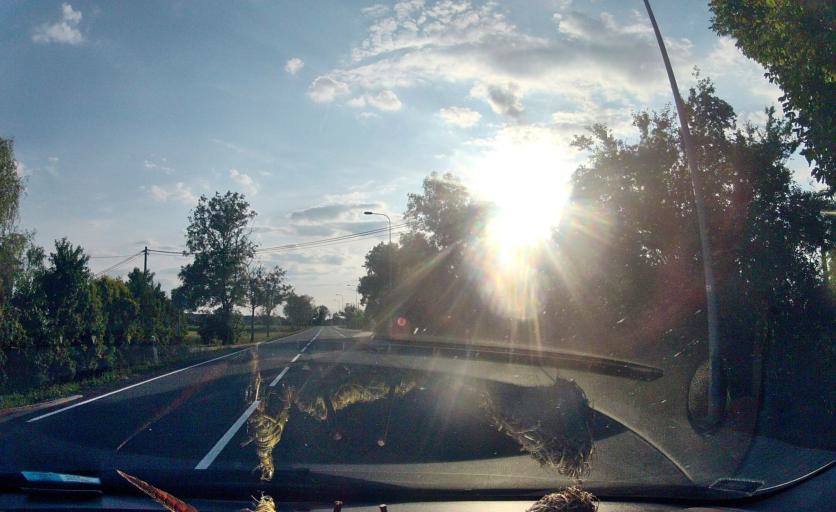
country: PL
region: Opole Voivodeship
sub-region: Powiat oleski
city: Gorzow Slaski
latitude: 51.0105
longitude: 18.3690
